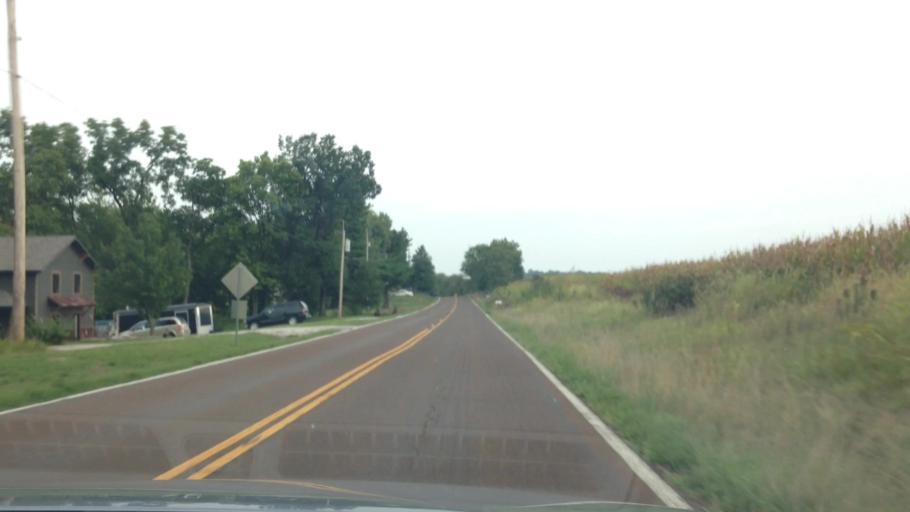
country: US
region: Missouri
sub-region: Clay County
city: Smithville
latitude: 39.4022
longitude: -94.5897
